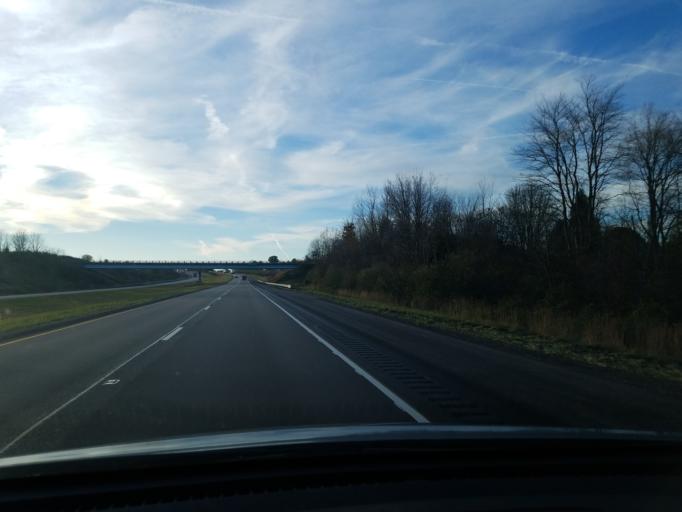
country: US
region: Indiana
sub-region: Dubois County
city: Ferdinand
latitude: 38.1997
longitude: -86.9208
